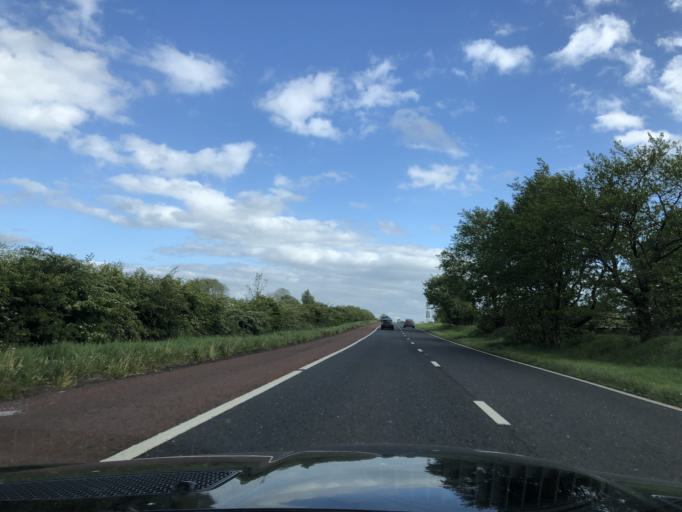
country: GB
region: Northern Ireland
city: Cullybackey
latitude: 54.9476
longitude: -6.3335
